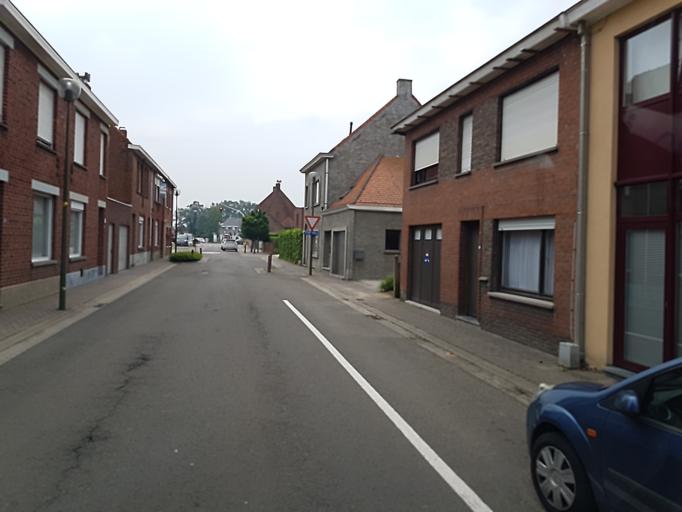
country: BE
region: Flanders
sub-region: Provincie West-Vlaanderen
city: Waregem
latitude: 50.9013
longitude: 3.4029
